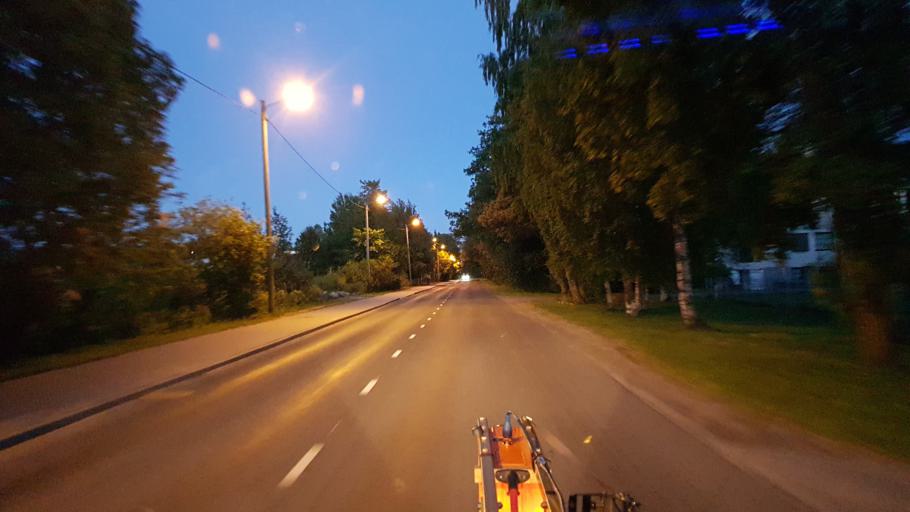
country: EE
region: Harju
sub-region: Harku vald
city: Tabasalu
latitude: 59.4391
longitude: 24.5982
